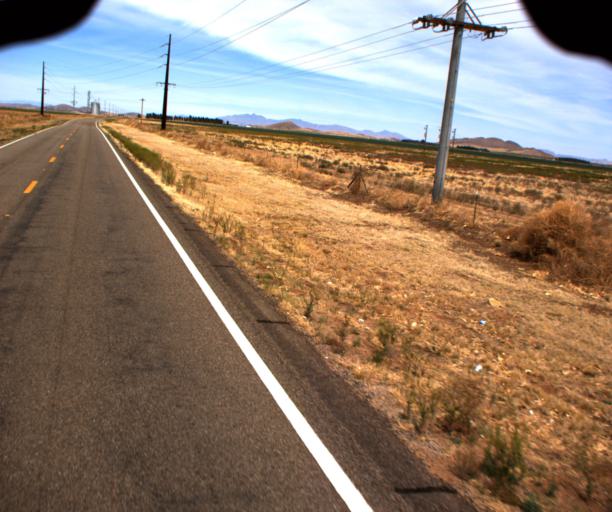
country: US
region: Arizona
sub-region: Cochise County
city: Tombstone
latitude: 31.8162
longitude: -109.6949
